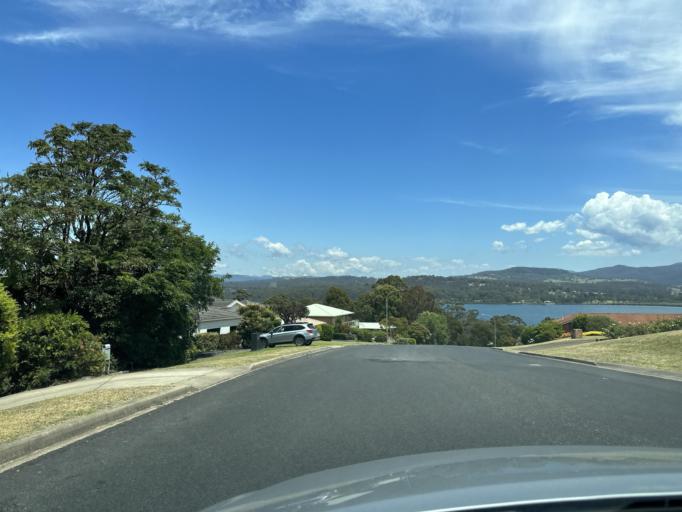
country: AU
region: New South Wales
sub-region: Bega Valley
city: Merimbula
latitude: -36.8919
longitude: 149.8954
